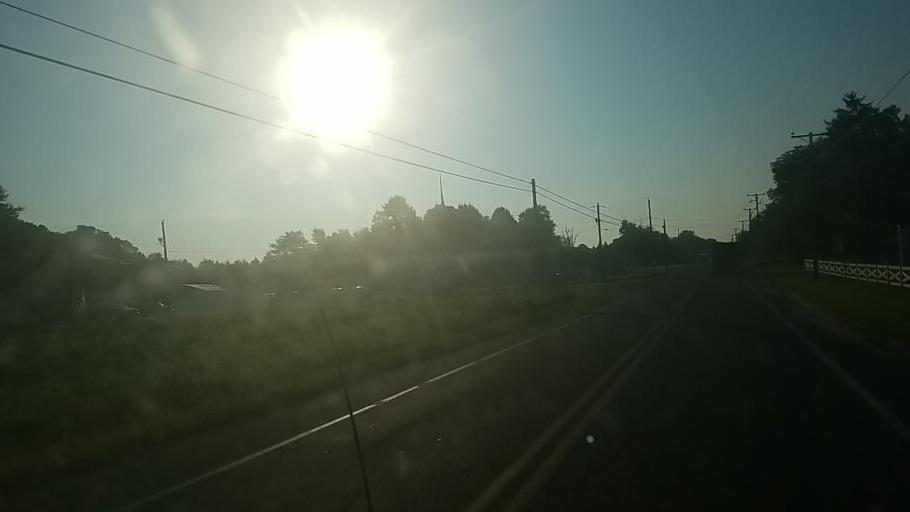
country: US
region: Maryland
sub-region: Worcester County
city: Ocean Pines
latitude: 38.4615
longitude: -75.1389
